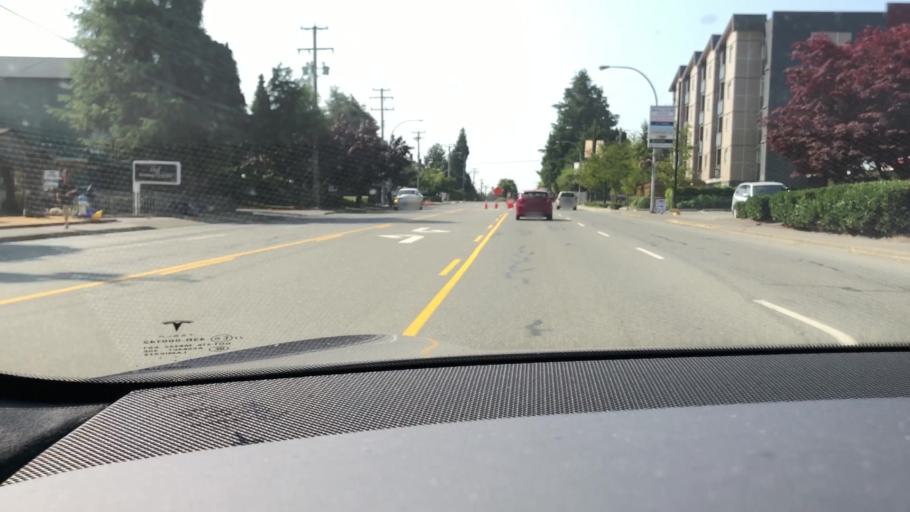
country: US
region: Washington
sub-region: Whatcom County
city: Point Roberts
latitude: 49.0307
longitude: -123.0687
